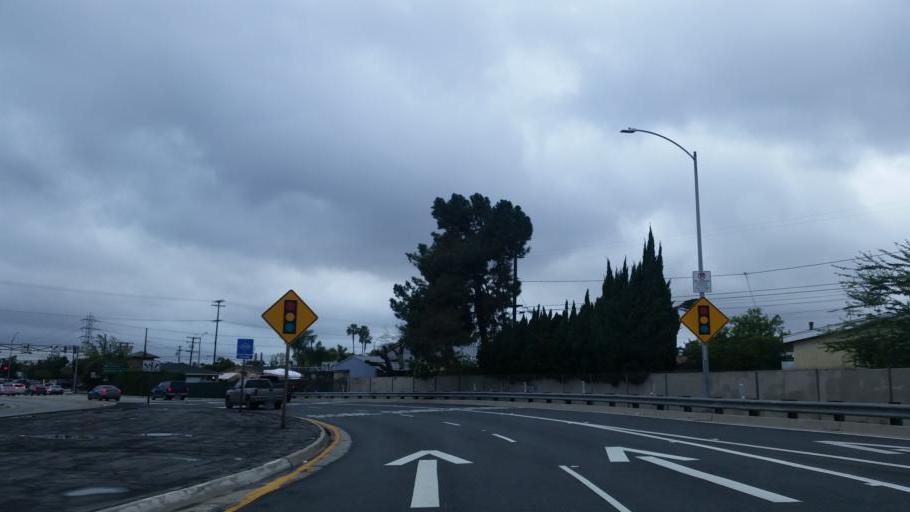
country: US
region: California
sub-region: Los Angeles County
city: Bellflower
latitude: 33.8889
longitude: -118.1055
